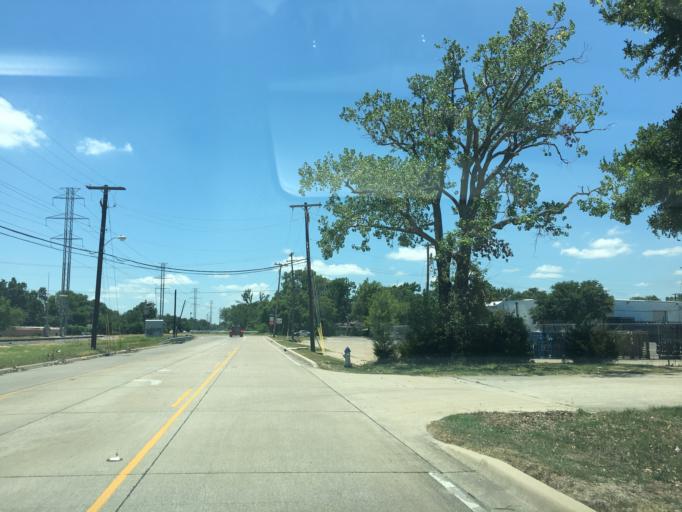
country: US
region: Texas
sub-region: Dallas County
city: Garland
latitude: 32.8441
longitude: -96.6849
